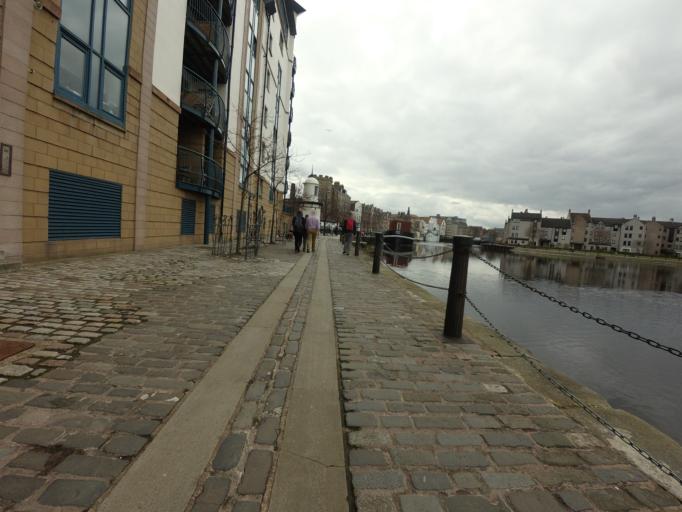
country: GB
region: Scotland
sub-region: West Lothian
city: Seafield
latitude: 55.9785
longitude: -3.1695
